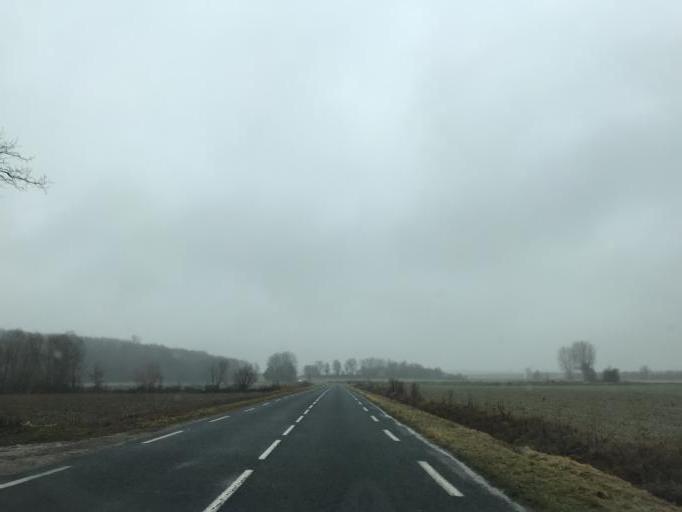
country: FR
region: Rhone-Alpes
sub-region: Departement de l'Ain
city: Miribel
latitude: 45.8505
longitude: 4.9330
